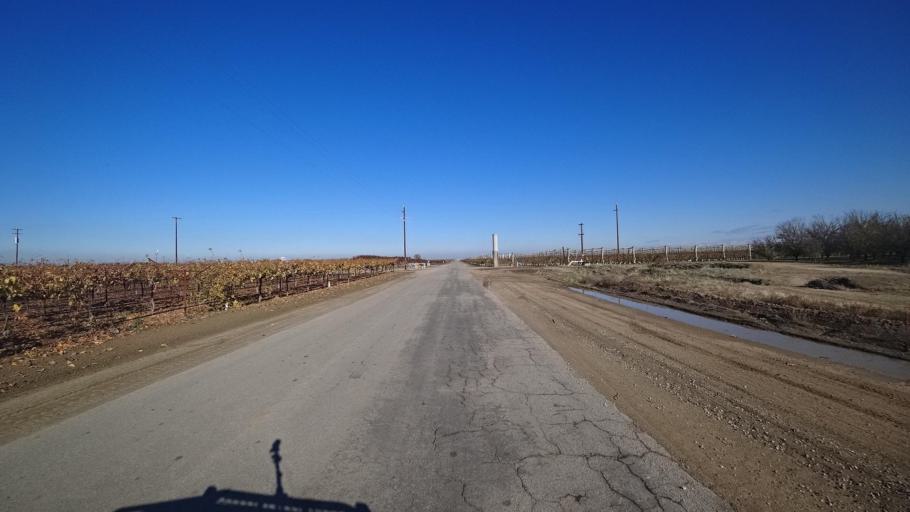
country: US
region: California
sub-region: Kern County
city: McFarland
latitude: 35.6953
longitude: -119.2673
